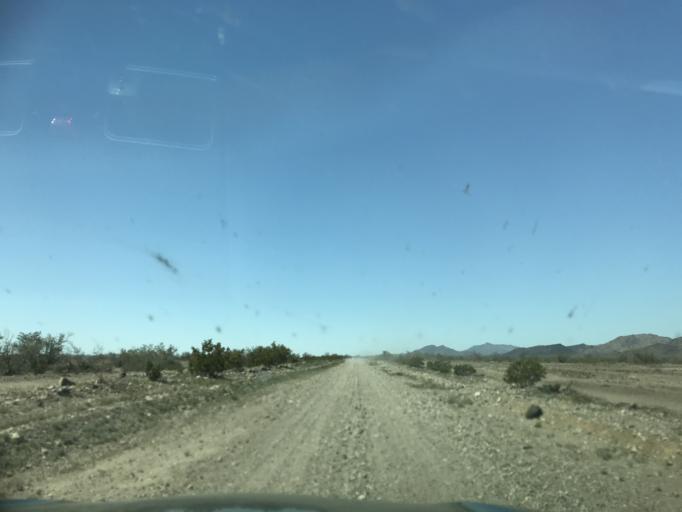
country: US
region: California
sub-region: Riverside County
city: Mesa Verde
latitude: 33.4787
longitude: -114.9360
